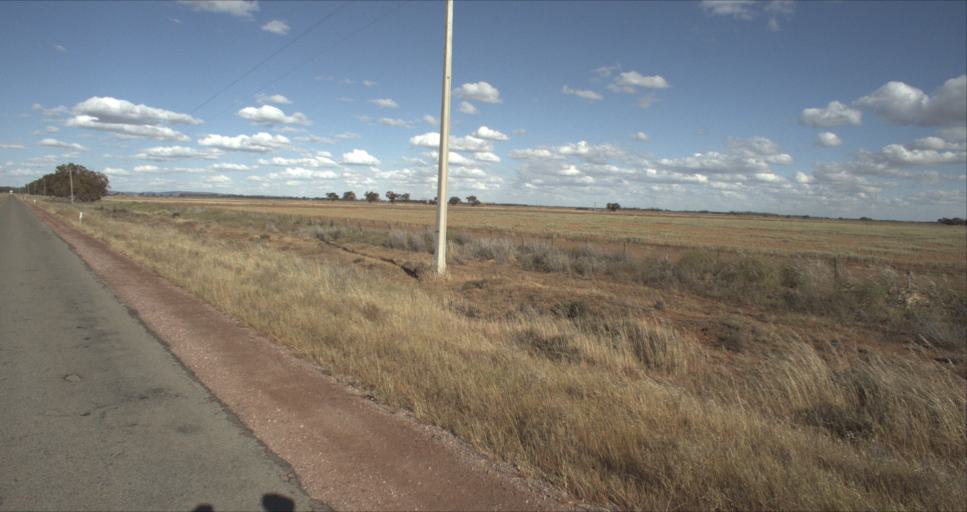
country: AU
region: New South Wales
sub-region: Leeton
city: Leeton
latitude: -34.4590
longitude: 146.2589
